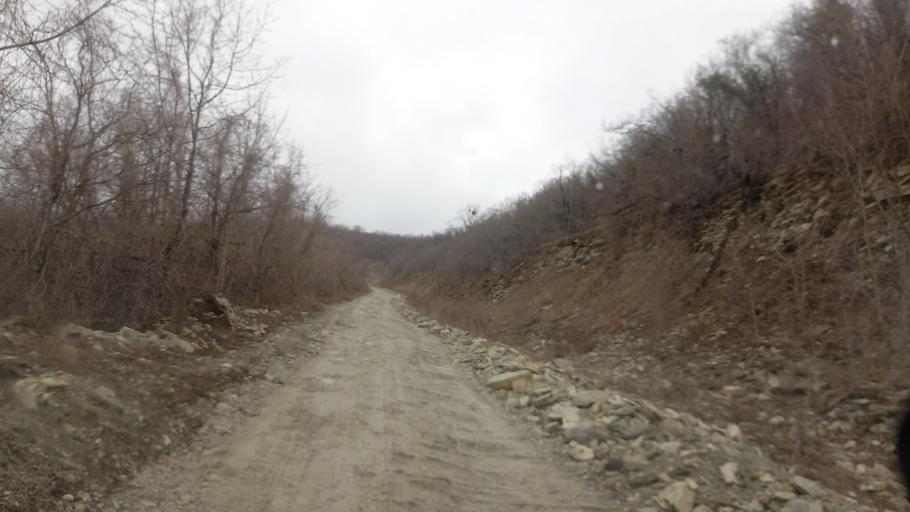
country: RU
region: Krasnodarskiy
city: Divnomorskoye
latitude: 44.5684
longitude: 38.2507
